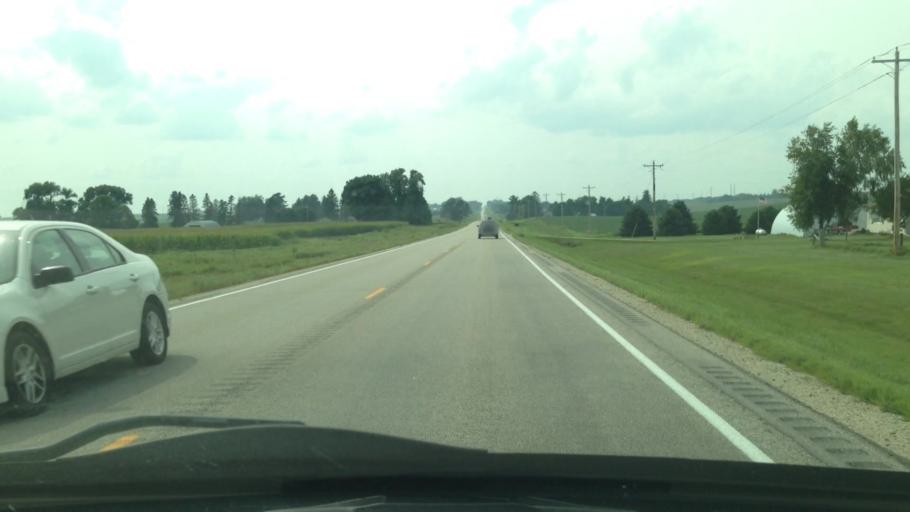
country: US
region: Minnesota
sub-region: Wabasha County
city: Elgin
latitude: 44.1657
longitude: -92.3497
